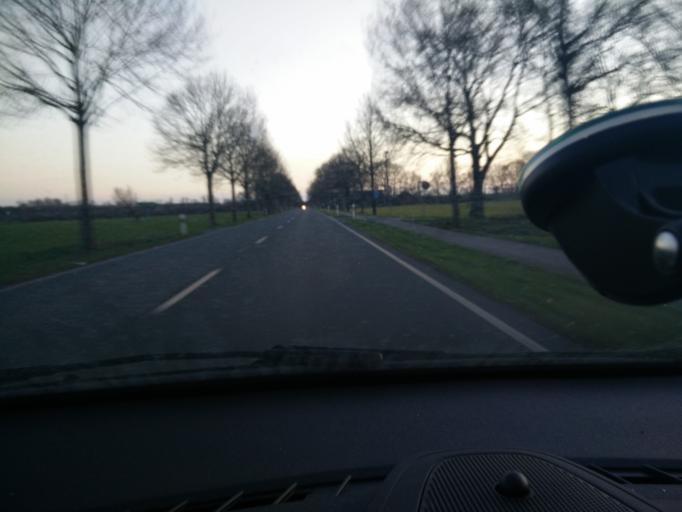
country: DE
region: North Rhine-Westphalia
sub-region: Regierungsbezirk Dusseldorf
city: Wesel
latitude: 51.7027
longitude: 6.6719
